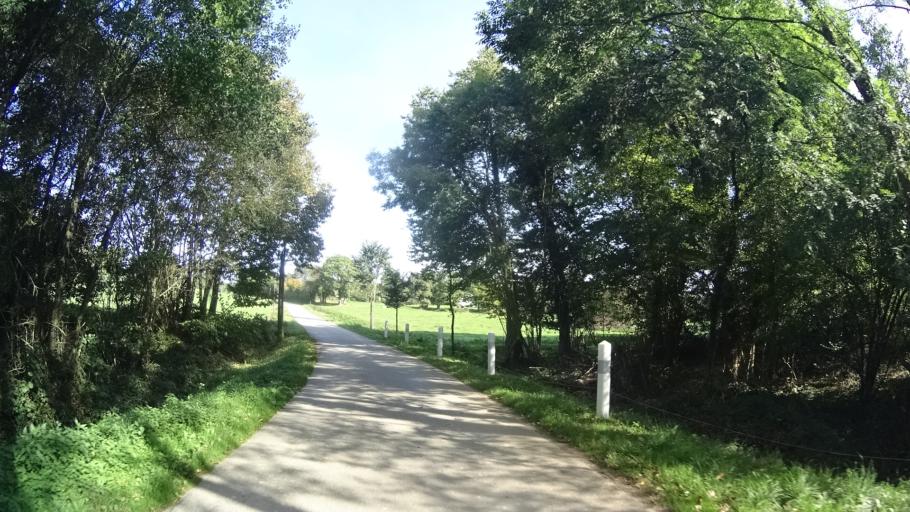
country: FR
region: Brittany
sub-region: Departement du Morbihan
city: La Gacilly
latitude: 47.7631
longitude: -2.1877
